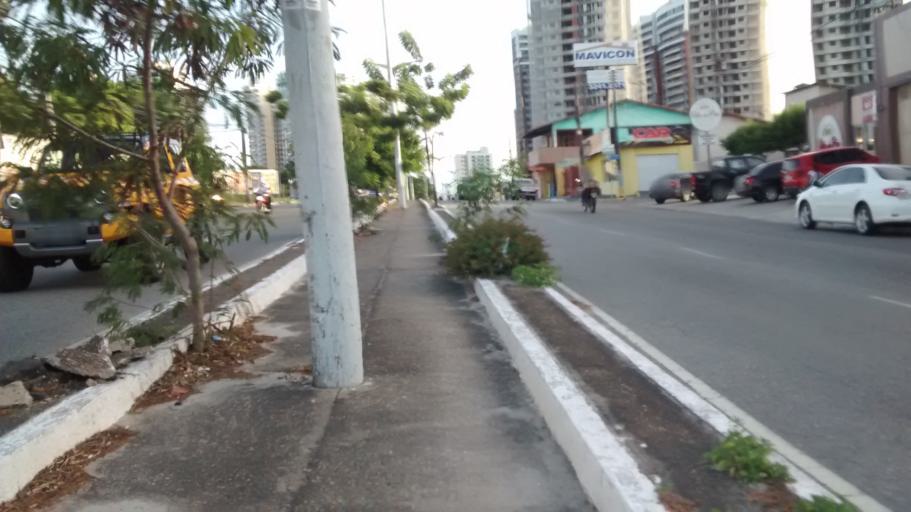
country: BR
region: Ceara
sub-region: Fortaleza
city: Fortaleza
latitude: -3.7624
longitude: -38.4938
